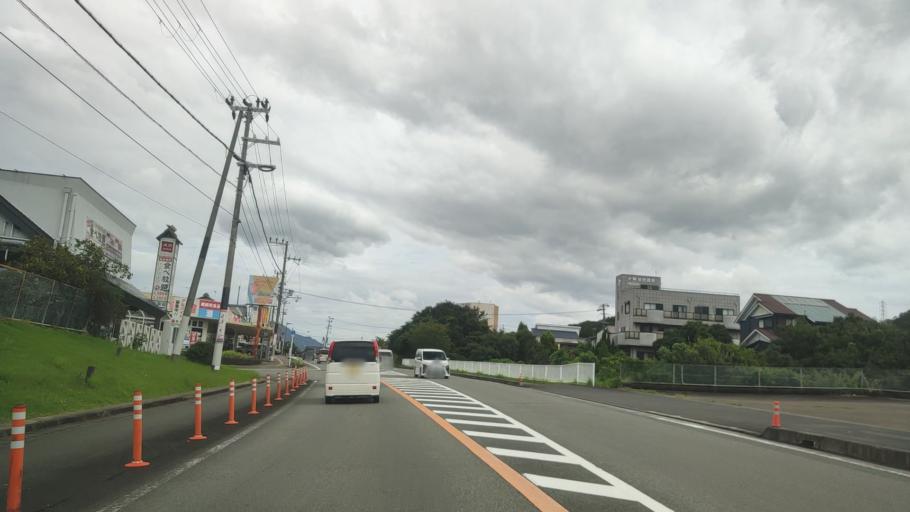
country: JP
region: Wakayama
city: Tanabe
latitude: 33.7066
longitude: 135.3996
